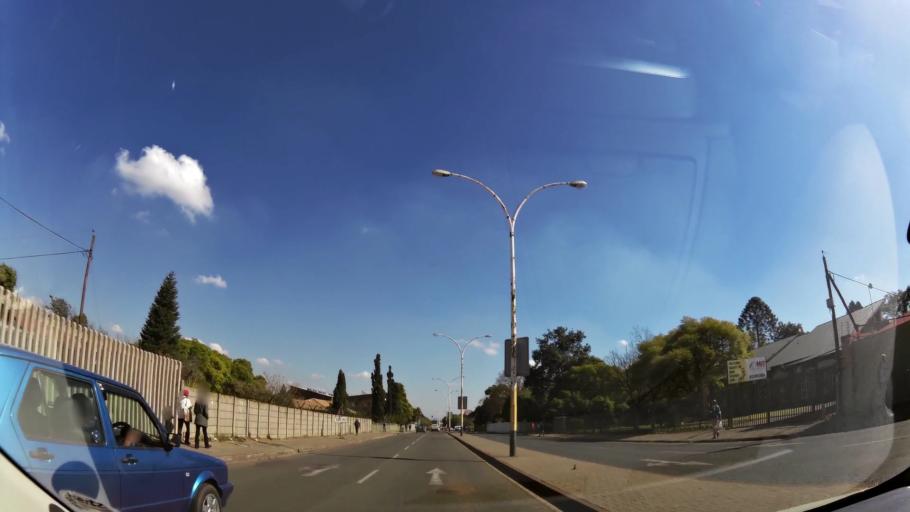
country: ZA
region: Mpumalanga
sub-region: Nkangala District Municipality
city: Witbank
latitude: -25.8756
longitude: 29.2261
